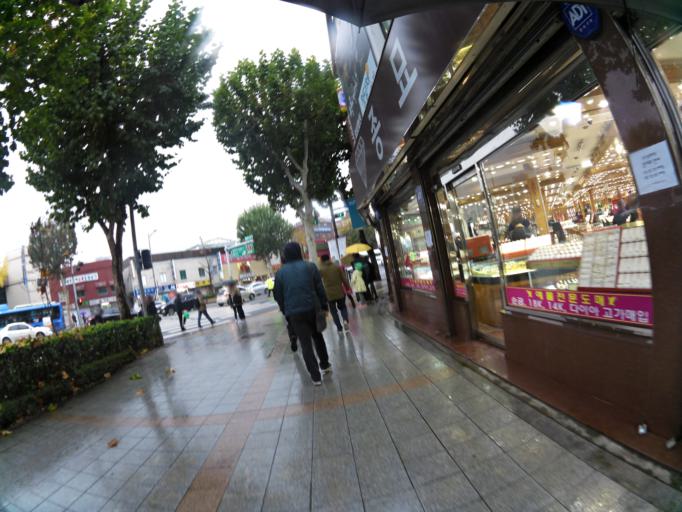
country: KR
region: Seoul
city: Seoul
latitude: 37.5710
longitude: 126.9971
